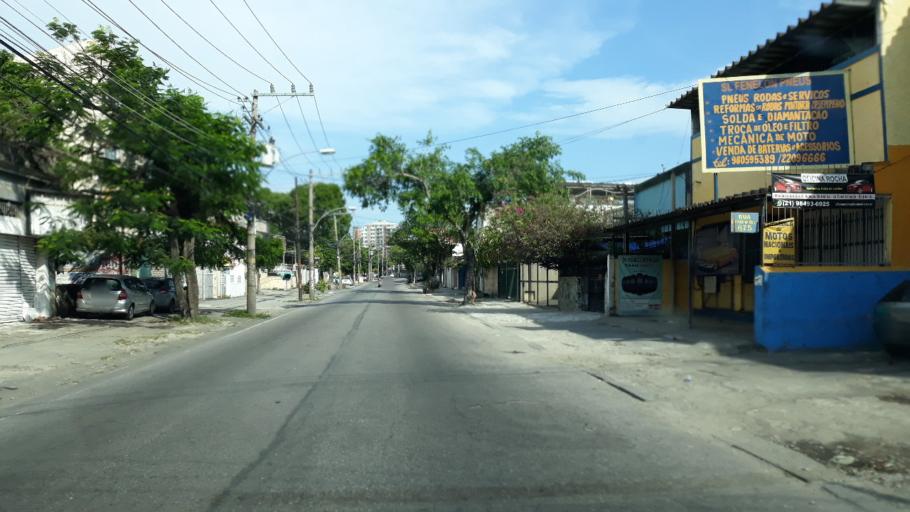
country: BR
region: Rio de Janeiro
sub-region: Duque De Caxias
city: Duque de Caxias
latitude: -22.8412
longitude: -43.2741
